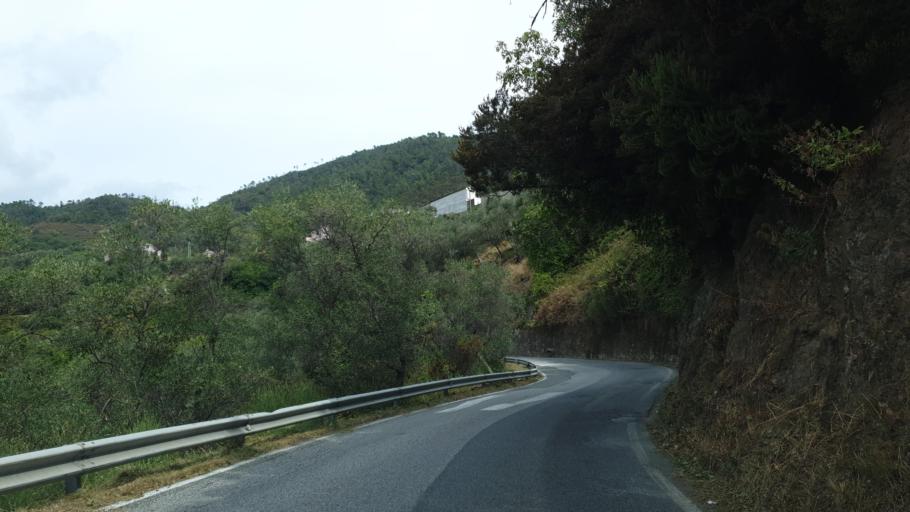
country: IT
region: Liguria
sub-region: Provincia di La Spezia
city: Levanto
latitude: 44.1916
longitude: 9.6282
